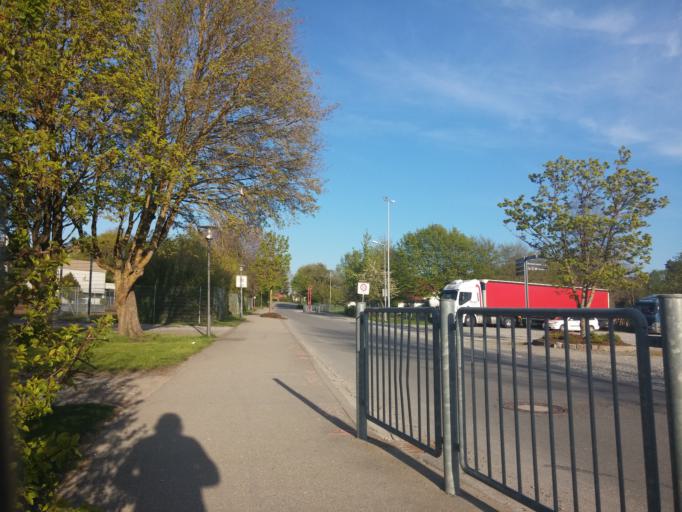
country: DE
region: Baden-Wuerttemberg
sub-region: Tuebingen Region
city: Bad Schussenried
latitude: 48.0049
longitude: 9.6497
